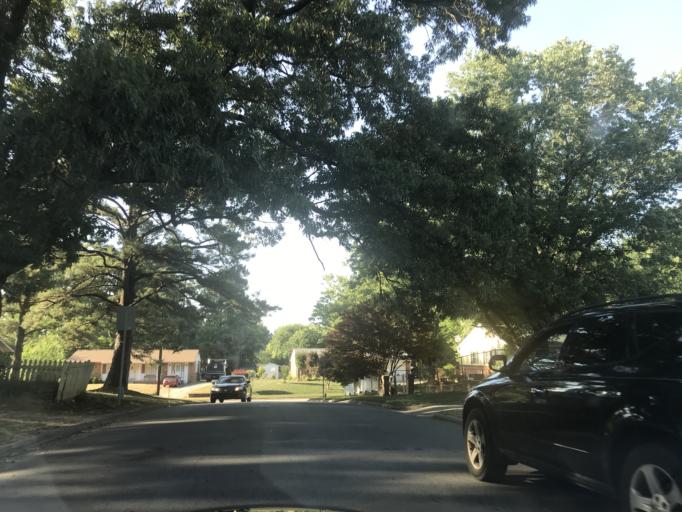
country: US
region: North Carolina
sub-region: Wake County
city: Garner
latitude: 35.7396
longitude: -78.6147
